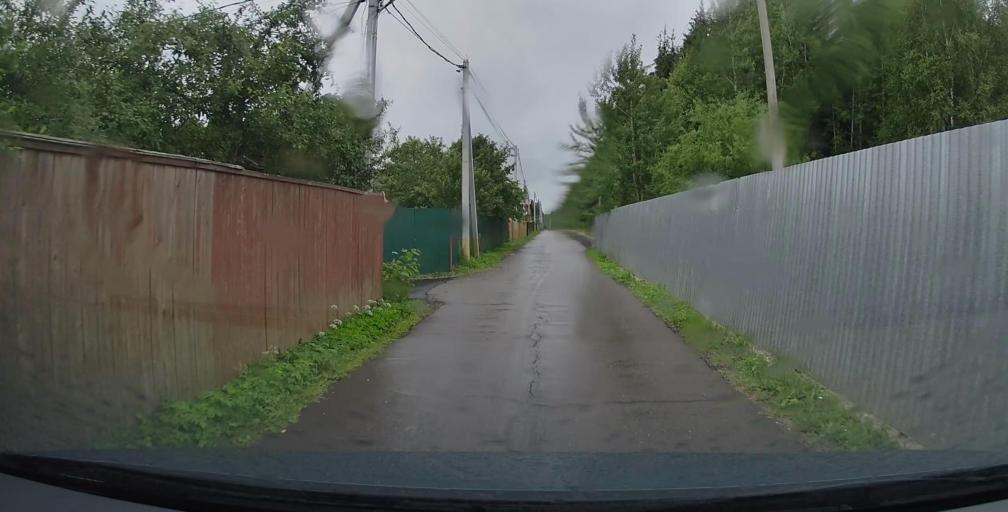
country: RU
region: Moskovskaya
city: Selyatino
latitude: 55.3931
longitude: 37.0182
